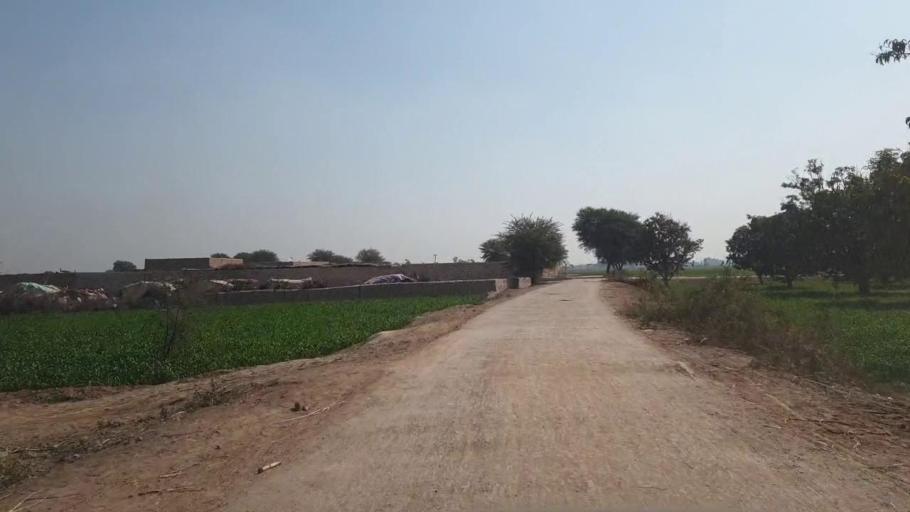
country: PK
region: Sindh
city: Tando Jam
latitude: 25.3283
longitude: 68.6325
